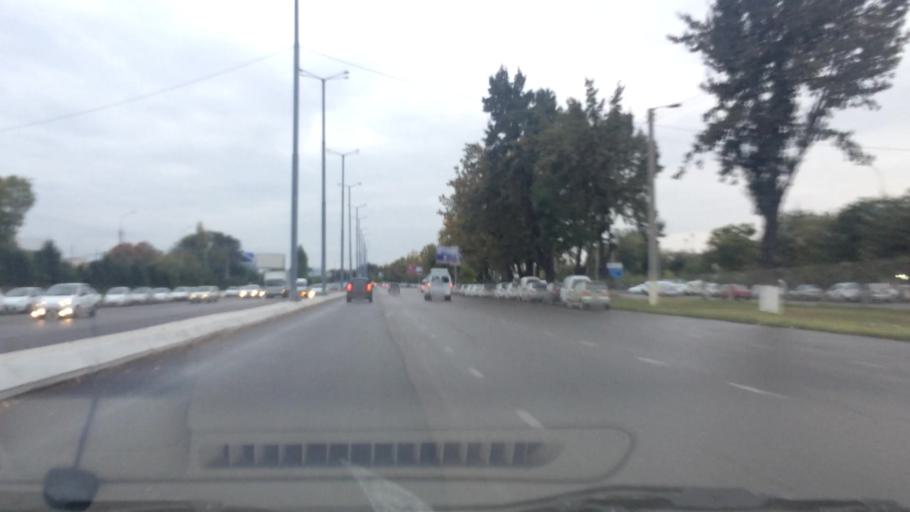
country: UZ
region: Toshkent Shahri
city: Tashkent
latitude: 41.2480
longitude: 69.1793
